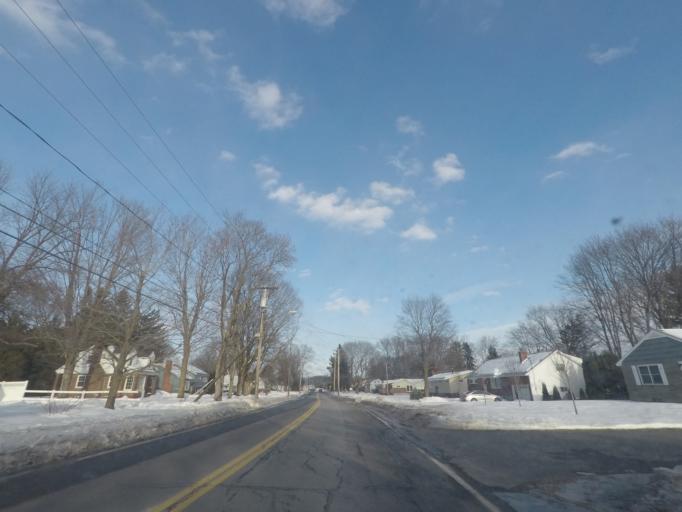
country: US
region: New York
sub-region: Schenectady County
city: Schenectady
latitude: 42.8319
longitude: -73.9365
